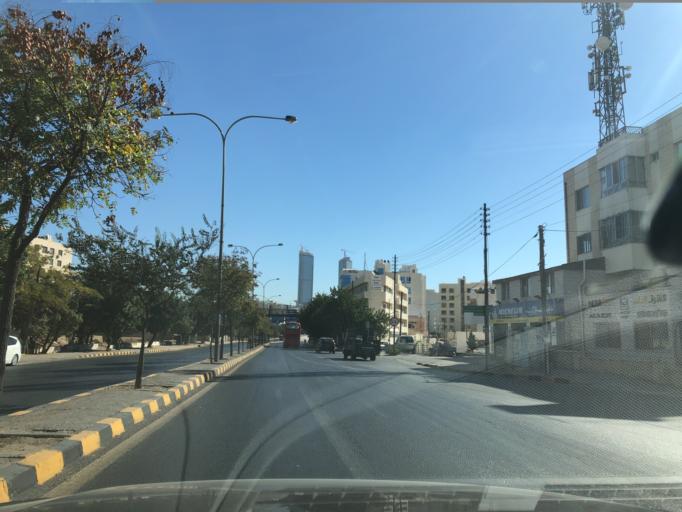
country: JO
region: Amman
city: Wadi as Sir
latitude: 31.9582
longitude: 35.8519
